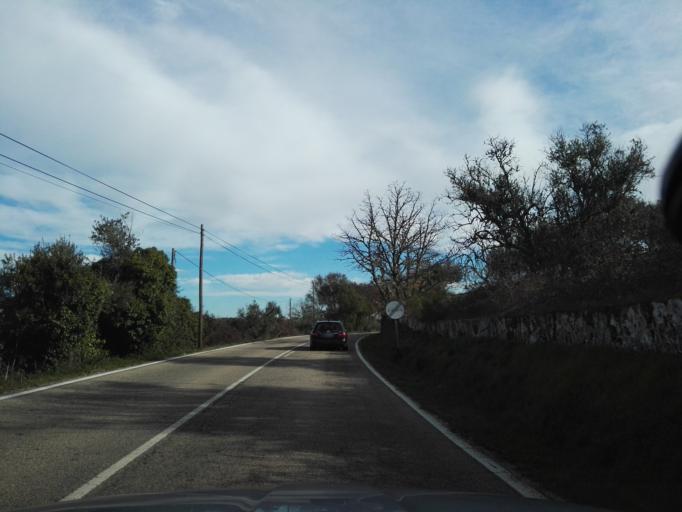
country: PT
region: Portalegre
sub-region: Nisa
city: Nisa
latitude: 39.5025
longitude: -7.6713
